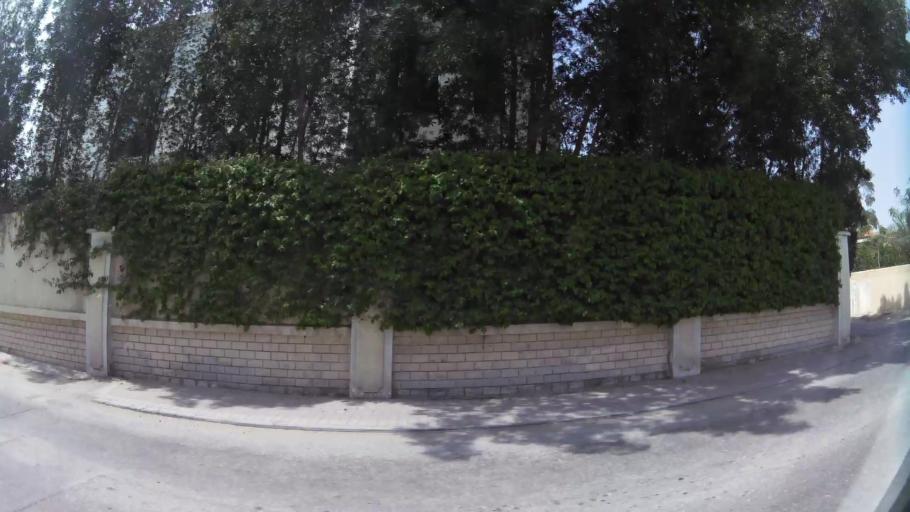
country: BH
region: Manama
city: Jidd Hafs
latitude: 26.2196
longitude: 50.4784
